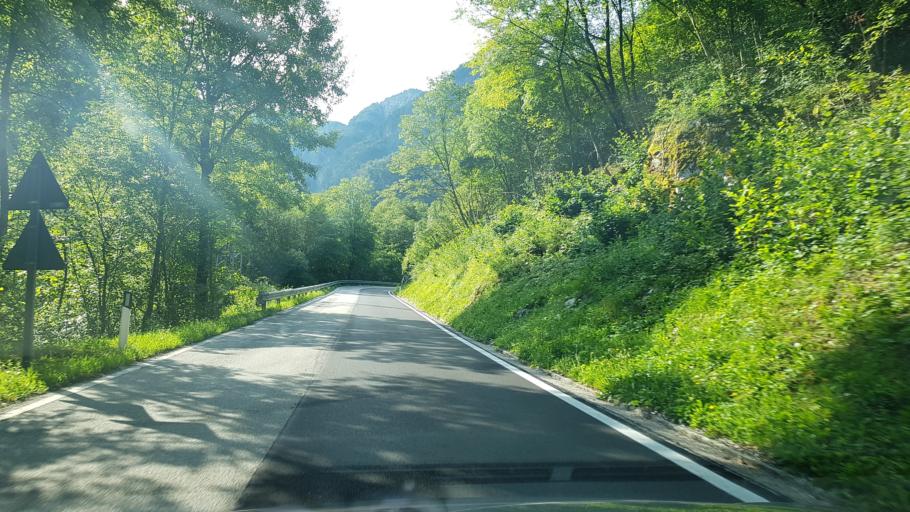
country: IT
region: Friuli Venezia Giulia
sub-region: Provincia di Udine
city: Chiusaforte
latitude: 46.4032
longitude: 13.3169
